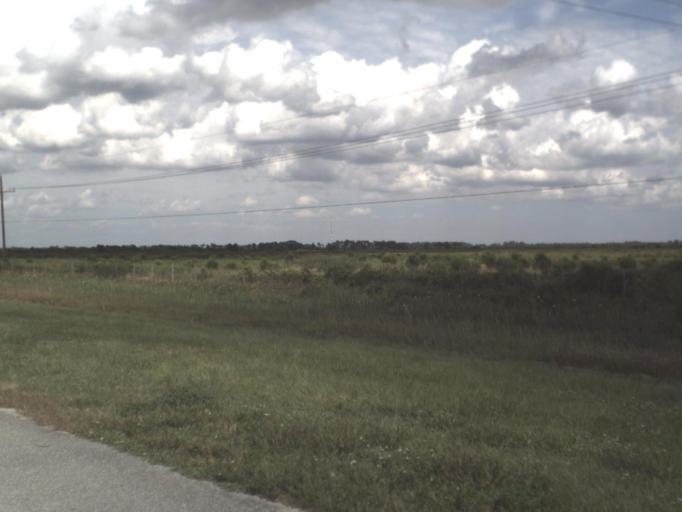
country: US
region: Florida
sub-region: Hendry County
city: Port LaBelle
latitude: 26.6281
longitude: -81.4364
